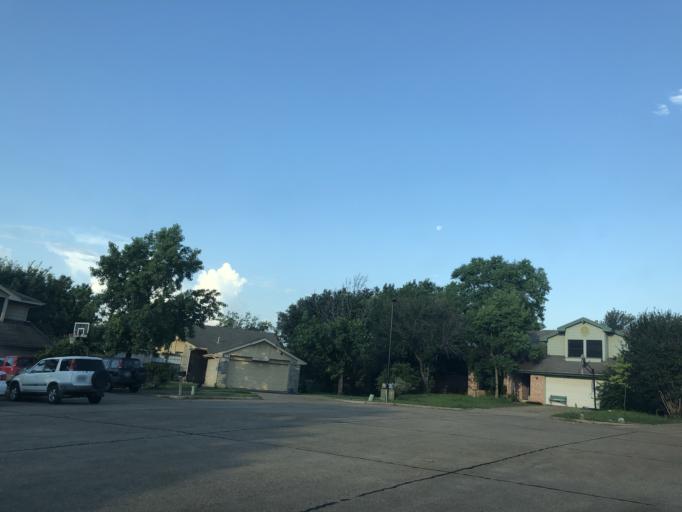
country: US
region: Texas
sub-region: Dallas County
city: Sunnyvale
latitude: 32.8420
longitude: -96.6080
